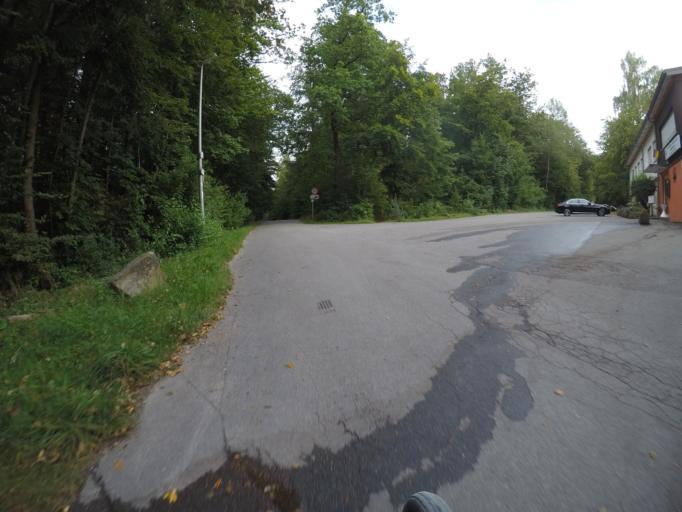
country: DE
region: Baden-Wuerttemberg
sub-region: Regierungsbezirk Stuttgart
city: Gerlingen
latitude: 48.7411
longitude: 9.0833
